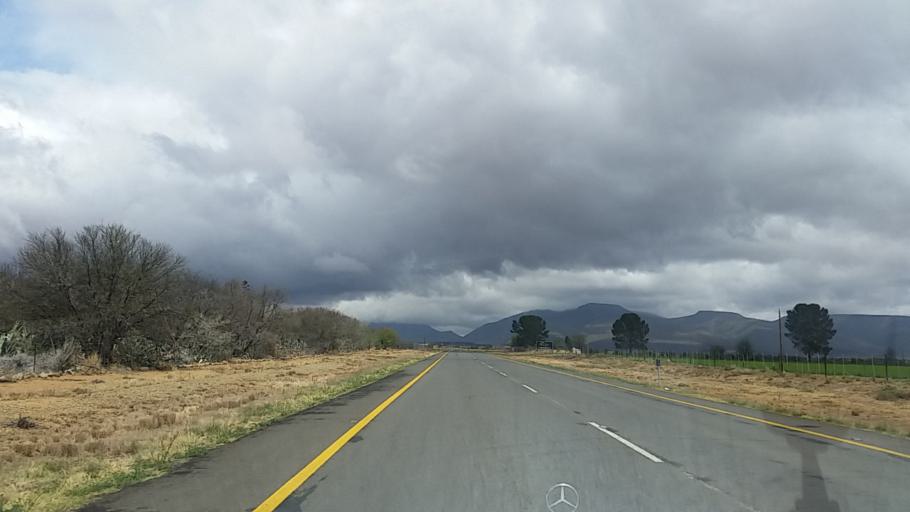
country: ZA
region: Eastern Cape
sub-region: Cacadu District Municipality
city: Graaff-Reinet
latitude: -32.1887
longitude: 24.5586
